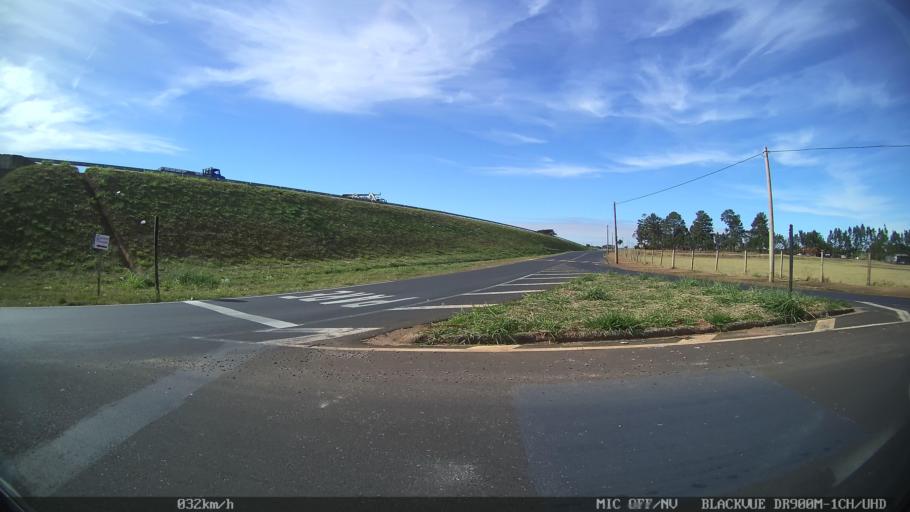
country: BR
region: Sao Paulo
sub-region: Guapiacu
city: Guapiacu
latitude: -20.7921
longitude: -49.2993
